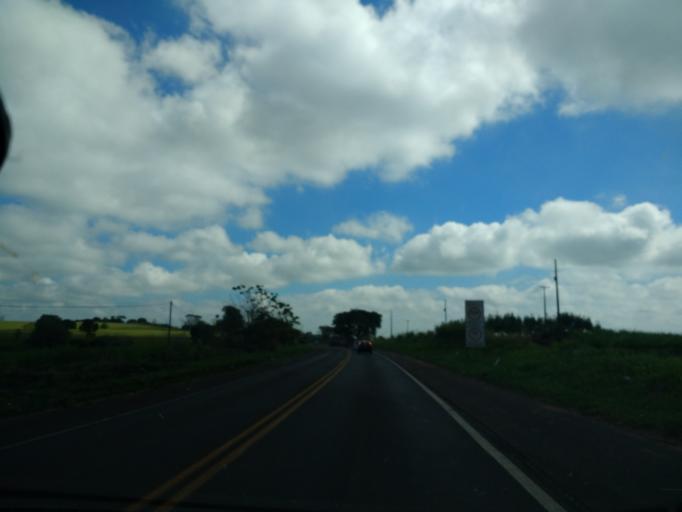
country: BR
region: Parana
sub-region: Cruzeiro Do Oeste
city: Cruzeiro do Oeste
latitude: -23.7662
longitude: -53.1166
